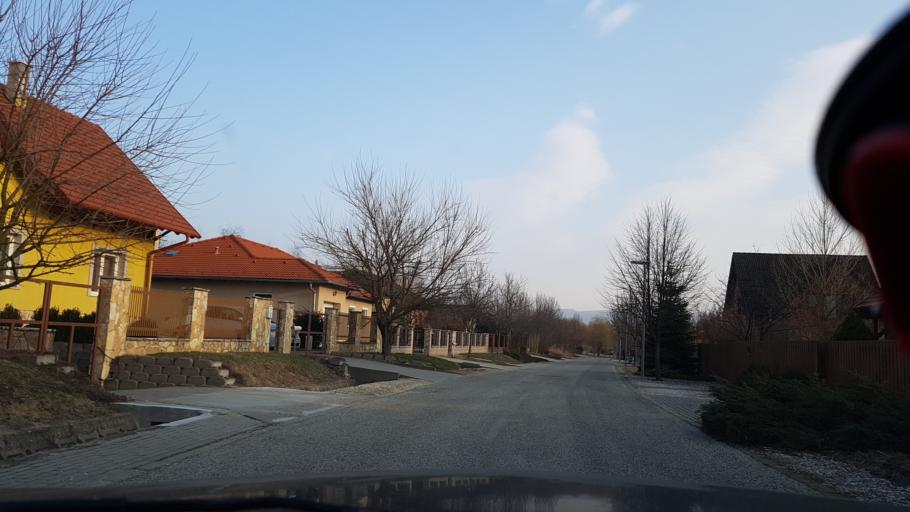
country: HU
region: Pest
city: Piliscsaba
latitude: 47.6456
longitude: 18.8141
